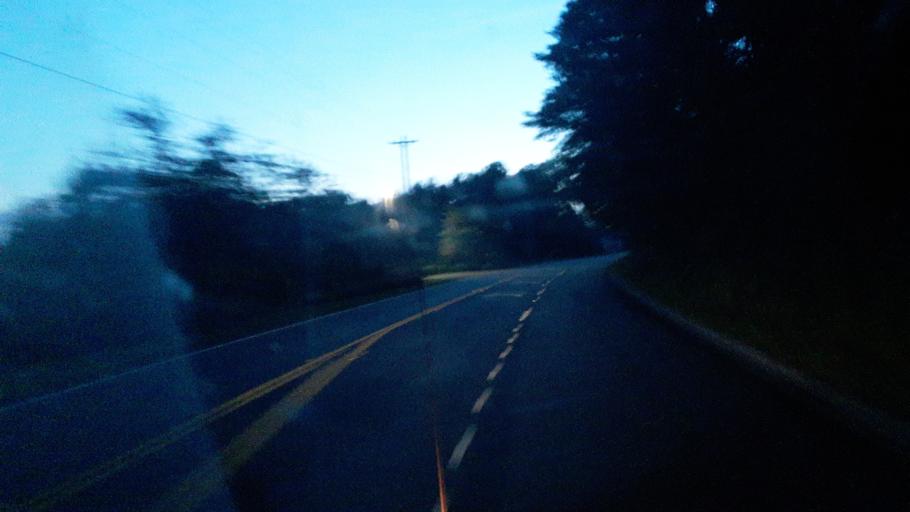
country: US
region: North Carolina
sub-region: Brunswick County
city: Carolina Shores
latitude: 33.8893
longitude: -78.5915
